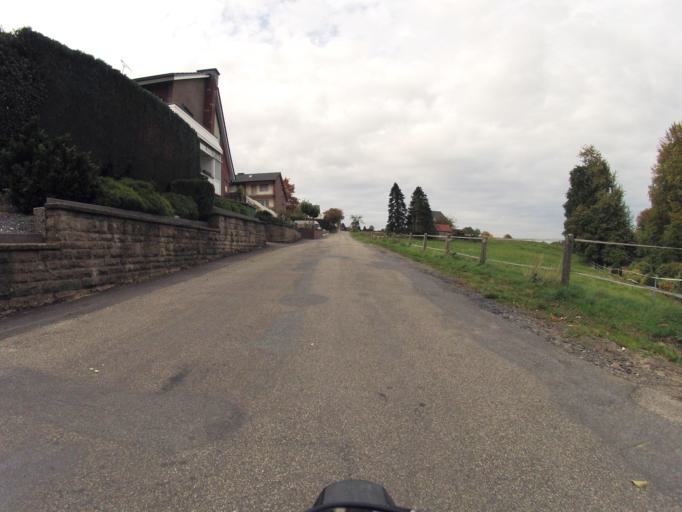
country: DE
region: North Rhine-Westphalia
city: Ibbenburen
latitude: 52.2974
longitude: 7.7469
